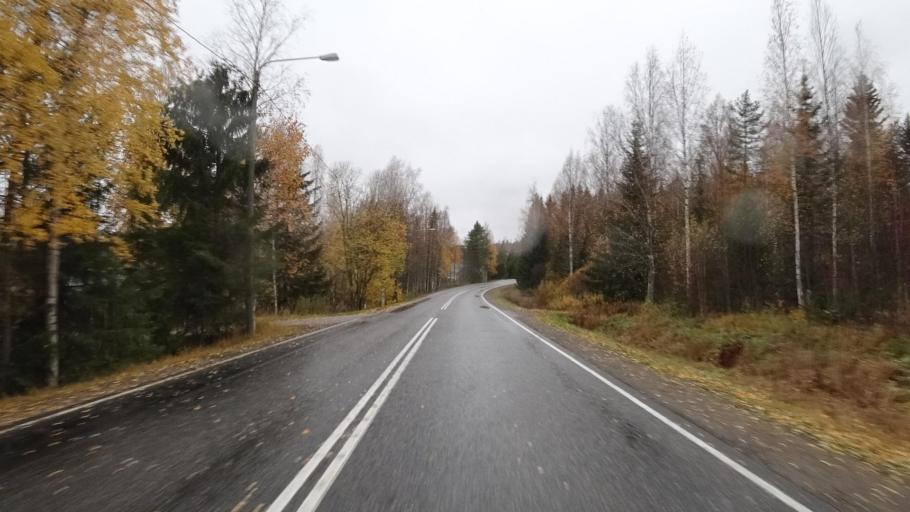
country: FI
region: Northern Savo
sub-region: Koillis-Savo
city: Tuusniemi
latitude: 62.7930
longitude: 28.5521
